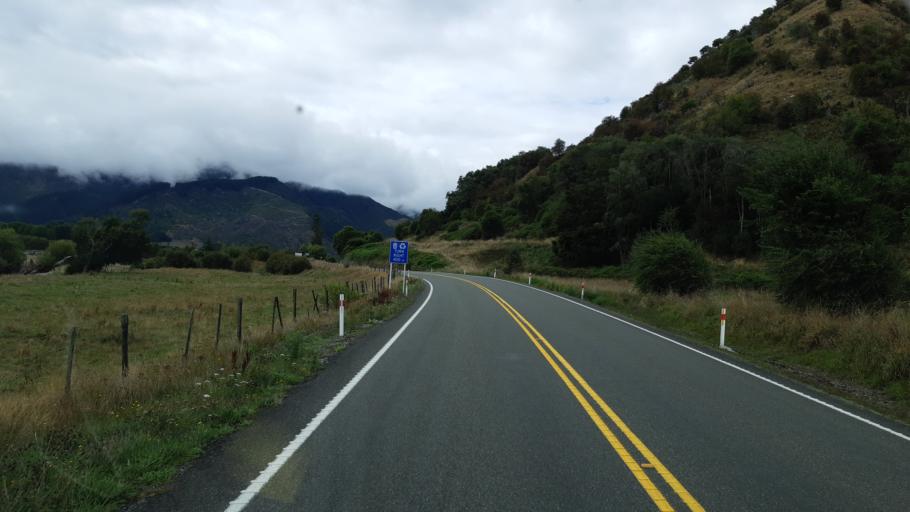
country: NZ
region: West Coast
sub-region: Buller District
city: Westport
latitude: -41.7962
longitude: 172.3096
